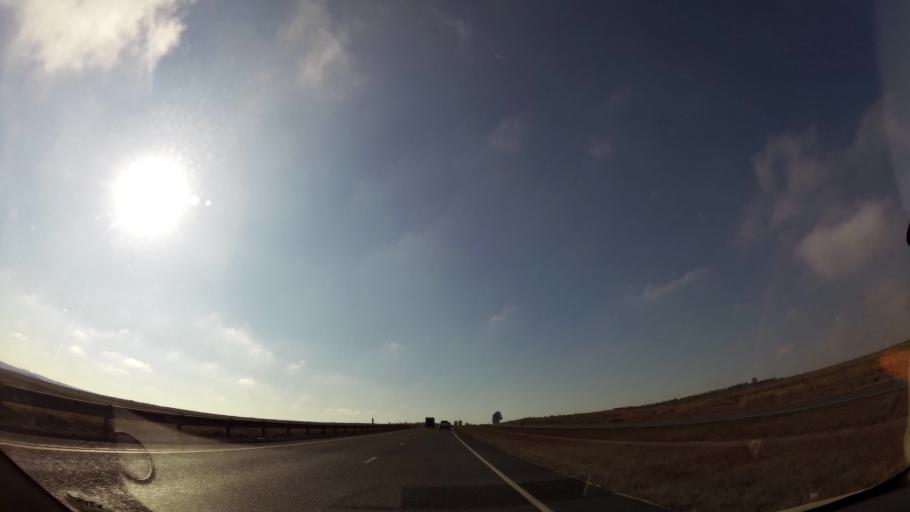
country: ZA
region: Mpumalanga
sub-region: Nkangala District Municipality
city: Delmas
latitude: -26.0184
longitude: 28.9043
